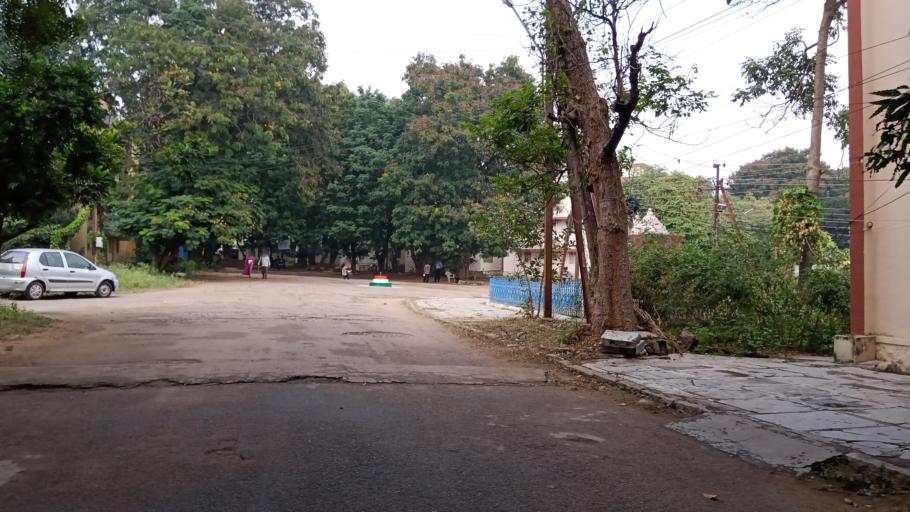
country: IN
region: Telangana
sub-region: Rangareddi
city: Kukatpalli
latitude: 17.4453
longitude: 78.4423
